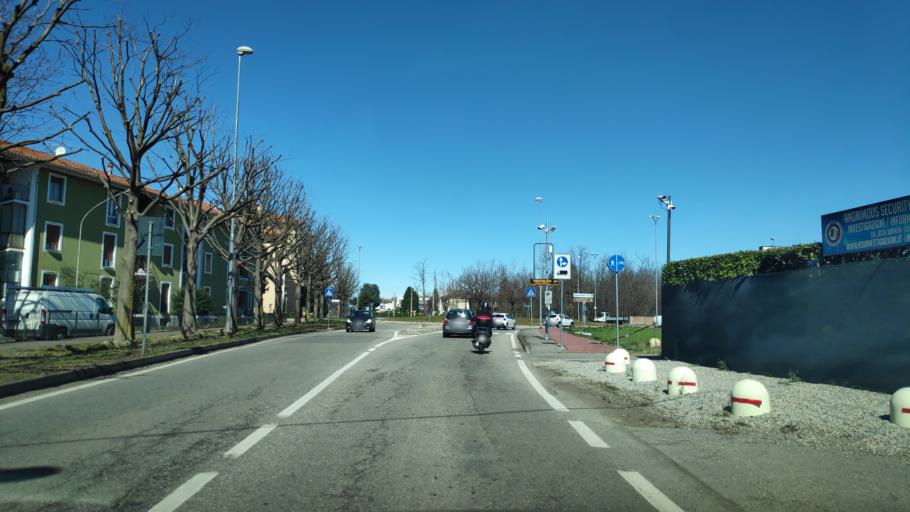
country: IT
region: Lombardy
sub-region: Provincia di Varese
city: Busto Arsizio
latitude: 45.6324
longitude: 8.8473
